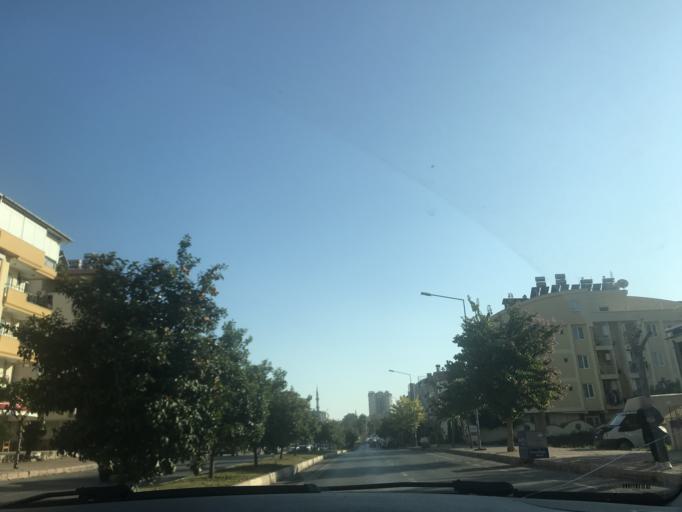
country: TR
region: Antalya
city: Antalya
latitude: 36.8860
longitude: 30.6474
